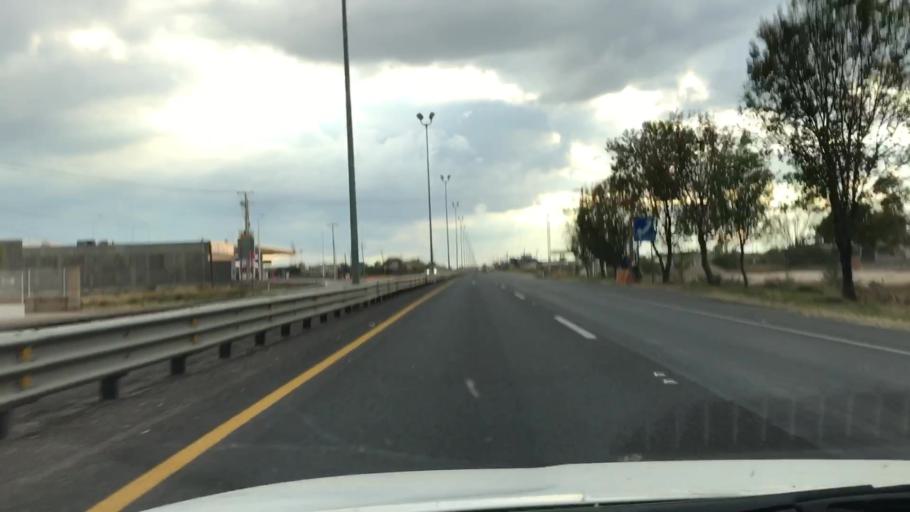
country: MX
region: Guanajuato
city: Penjamo
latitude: 20.4324
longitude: -101.7023
